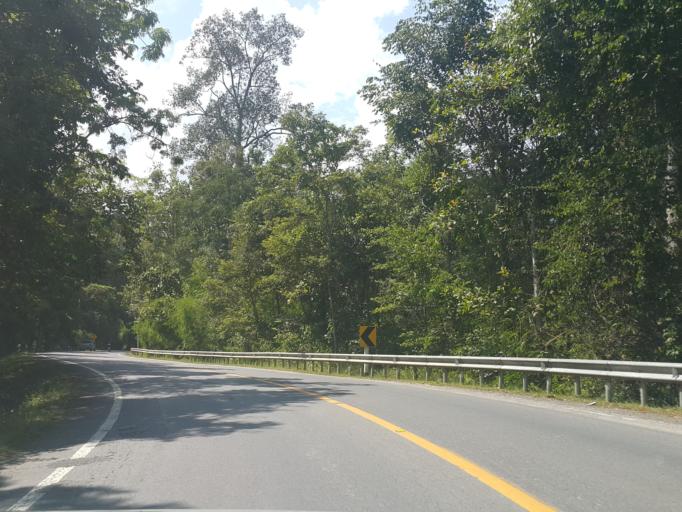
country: TH
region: Chiang Mai
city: Chom Thong
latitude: 18.5295
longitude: 98.6248
